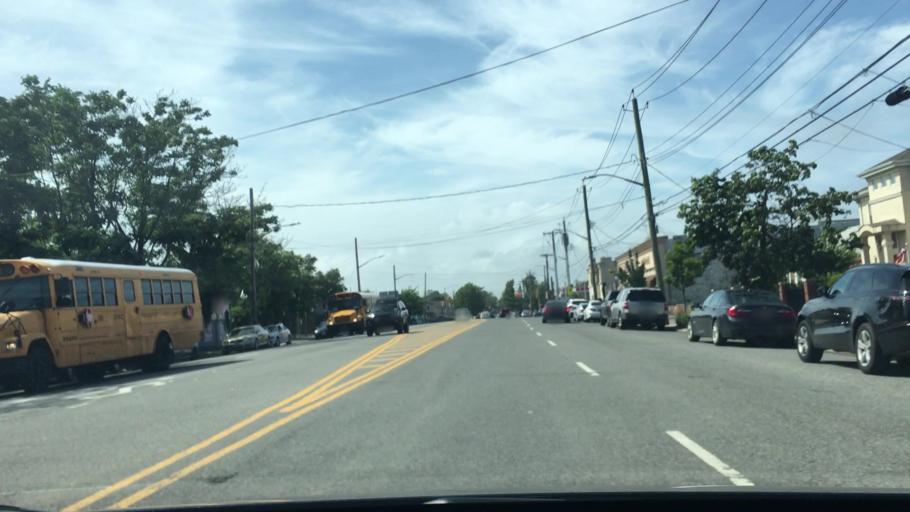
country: US
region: New York
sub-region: Kings County
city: Brooklyn
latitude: 40.6141
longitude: -73.9124
